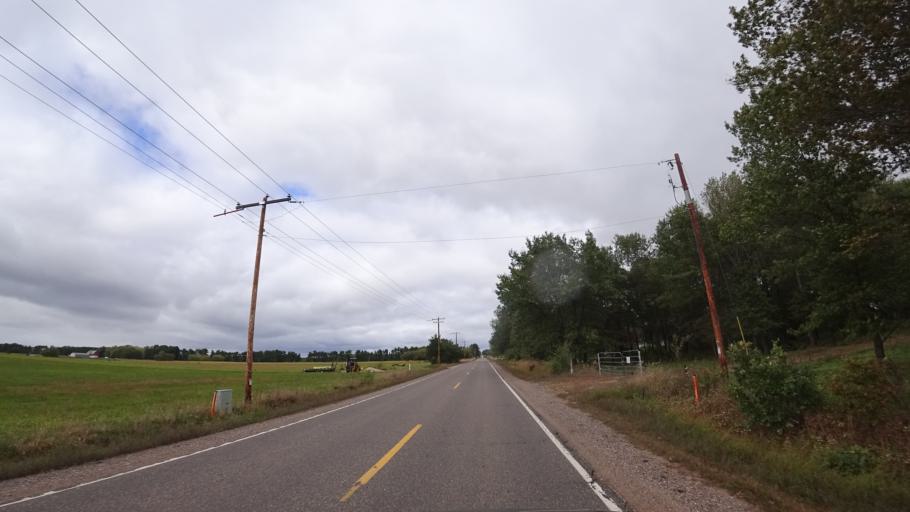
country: US
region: Wisconsin
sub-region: Chippewa County
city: Lake Wissota
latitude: 44.9756
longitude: -91.2678
